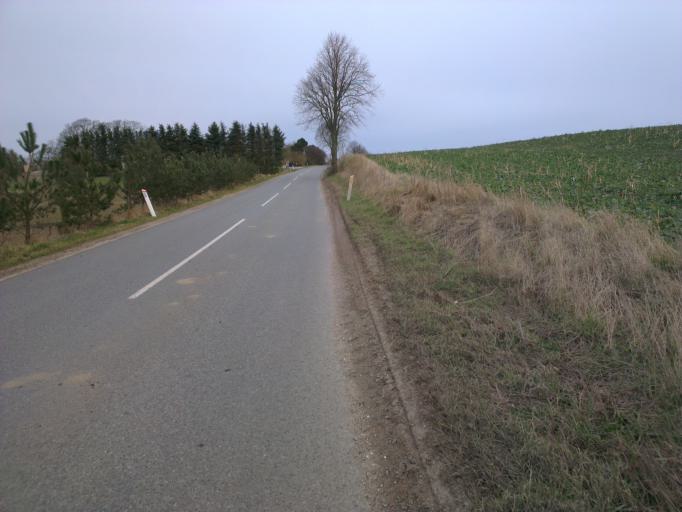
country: DK
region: Capital Region
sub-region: Frederikssund Kommune
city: Skibby
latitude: 55.7846
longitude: 11.9174
